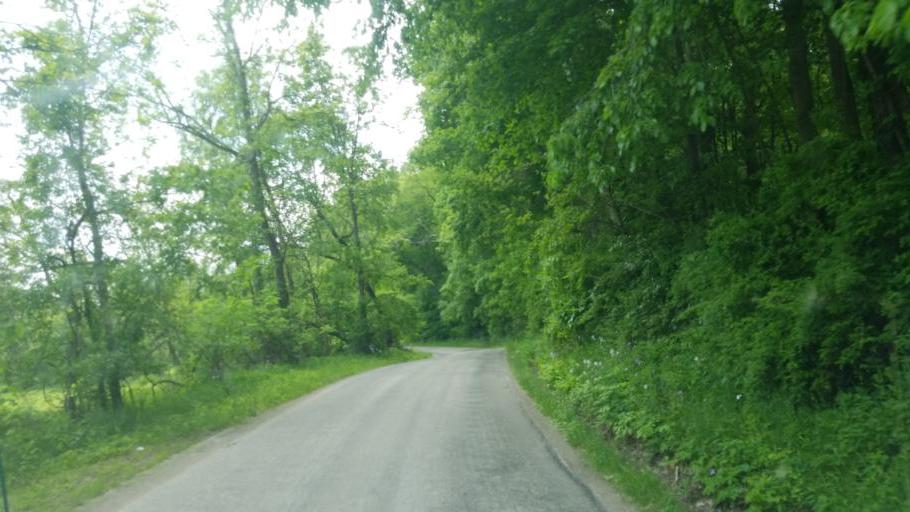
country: US
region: Ohio
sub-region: Ashland County
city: Ashland
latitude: 40.7594
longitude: -82.3495
